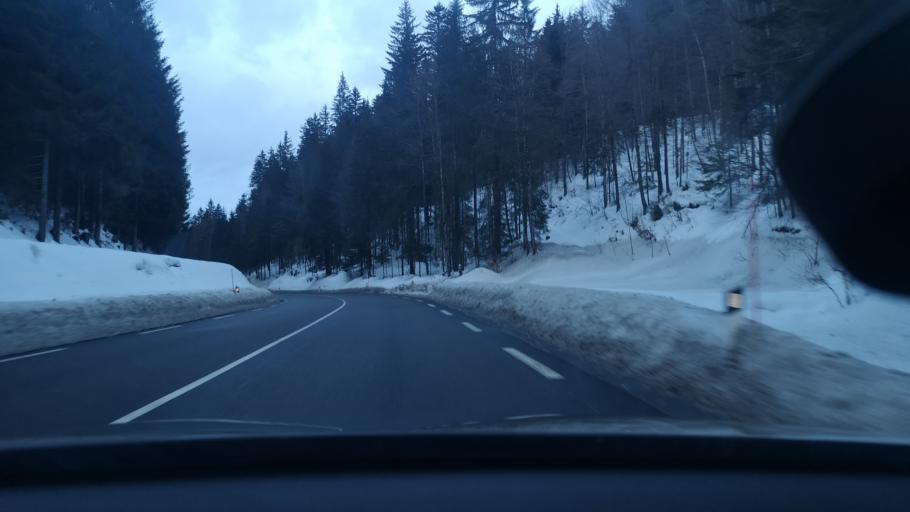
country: FR
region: Franche-Comte
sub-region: Departement du Doubs
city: Jougne
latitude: 46.8026
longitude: 6.3579
